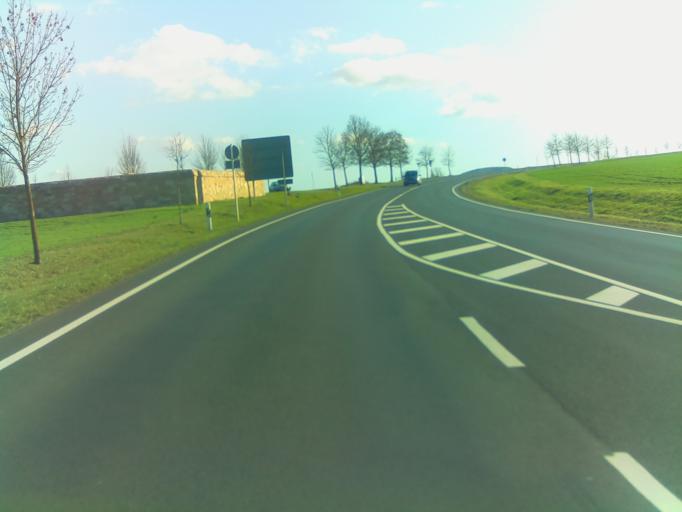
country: DE
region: Bavaria
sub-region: Regierungsbezirk Unterfranken
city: Wuelfershausen
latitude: 50.3279
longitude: 10.3383
